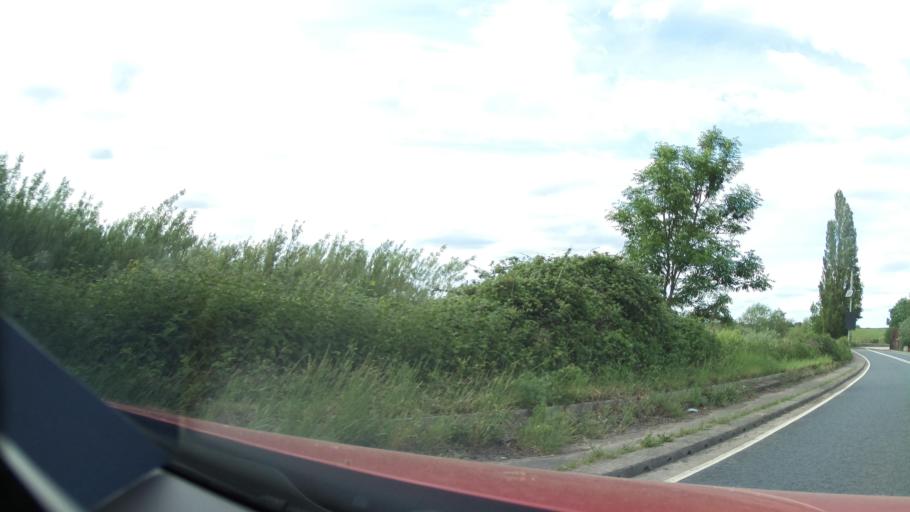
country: GB
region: England
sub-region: Worcestershire
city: Bransford
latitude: 52.1752
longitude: -2.2888
